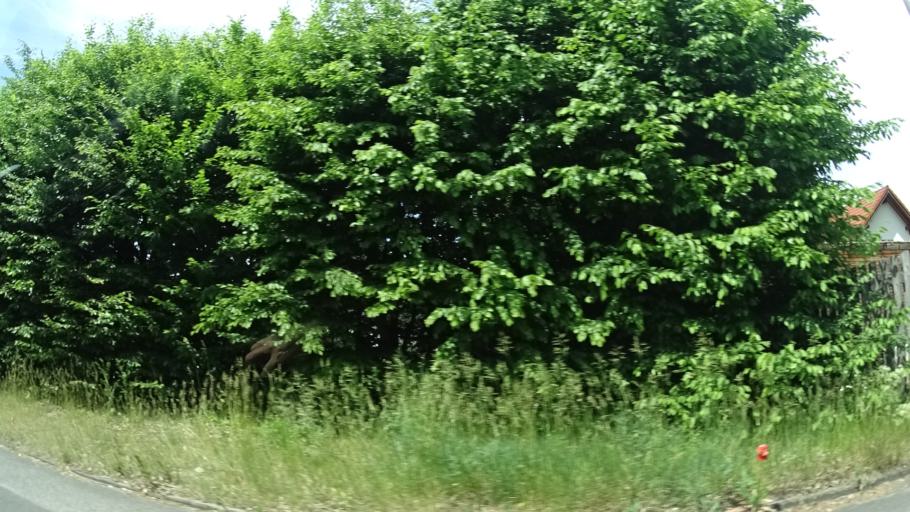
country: DE
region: Bavaria
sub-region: Regierungsbezirk Unterfranken
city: Salz
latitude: 50.3129
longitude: 10.2180
